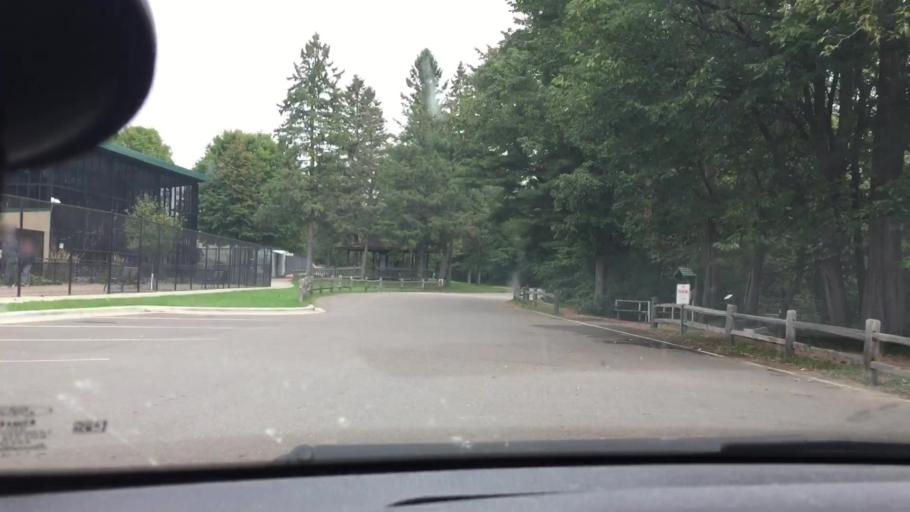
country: US
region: Wisconsin
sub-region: Chippewa County
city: Chippewa Falls
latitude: 44.9496
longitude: -91.3996
